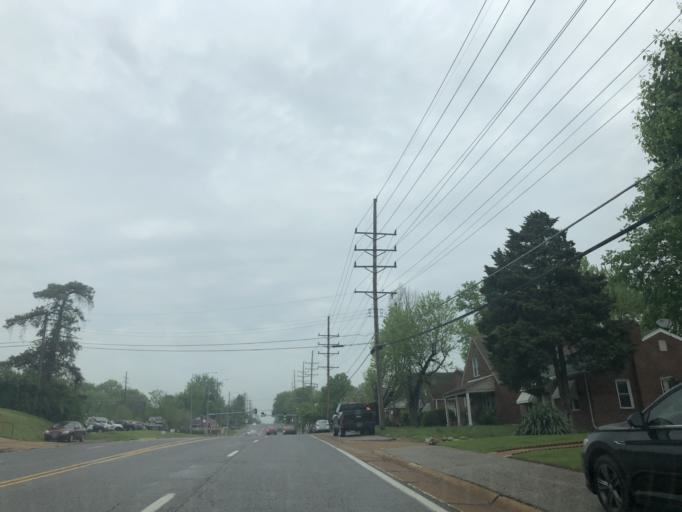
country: US
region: Missouri
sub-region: Saint Louis County
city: Marlborough
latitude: 38.5640
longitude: -90.3210
